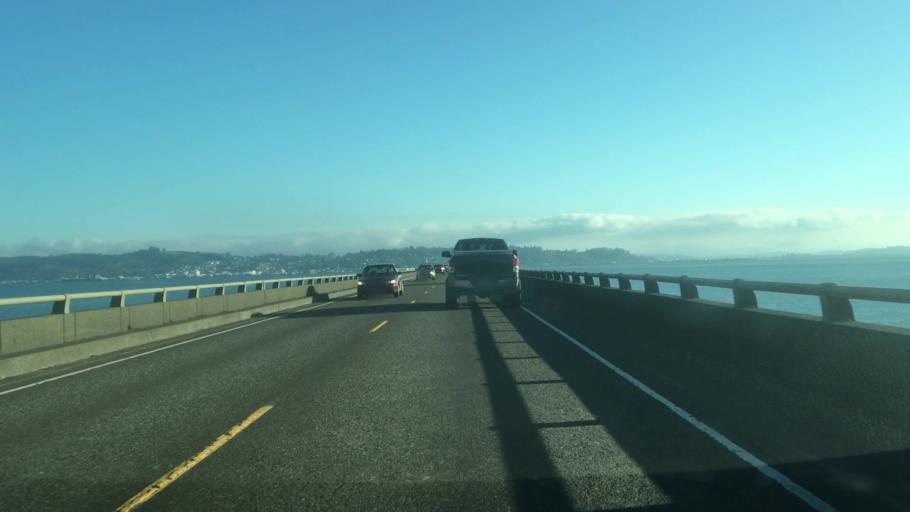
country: US
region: Oregon
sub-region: Clatsop County
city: Astoria
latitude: 46.2269
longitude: -123.8678
